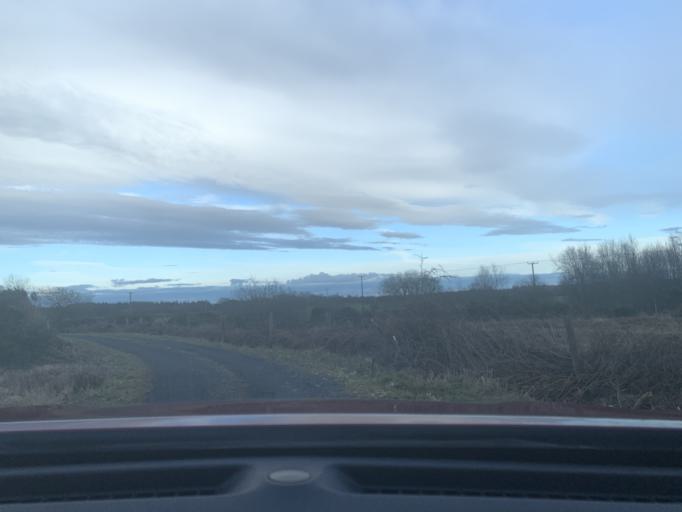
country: IE
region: Connaught
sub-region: Roscommon
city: Ballaghaderreen
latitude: 53.8873
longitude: -8.5742
